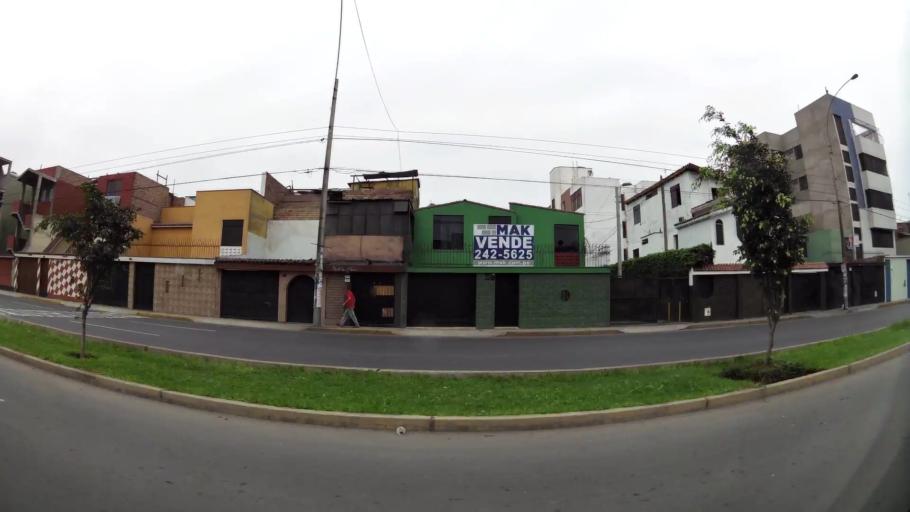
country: PE
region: Callao
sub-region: Callao
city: Callao
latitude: -12.0546
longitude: -77.0800
